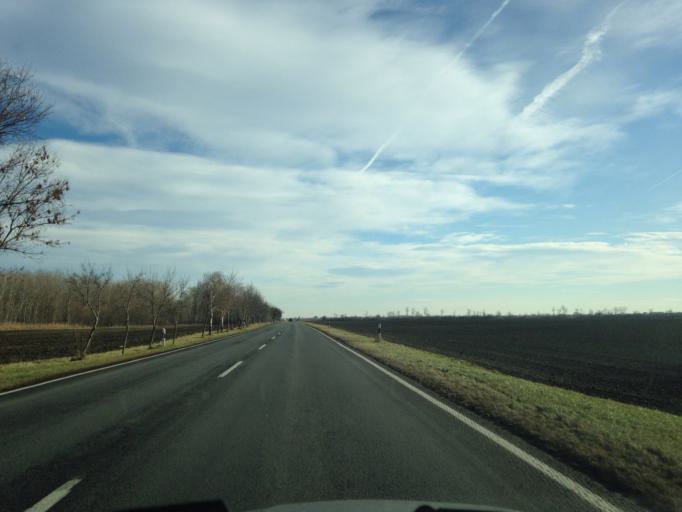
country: HU
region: Gyor-Moson-Sopron
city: Kimle
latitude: 47.8179
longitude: 17.3387
